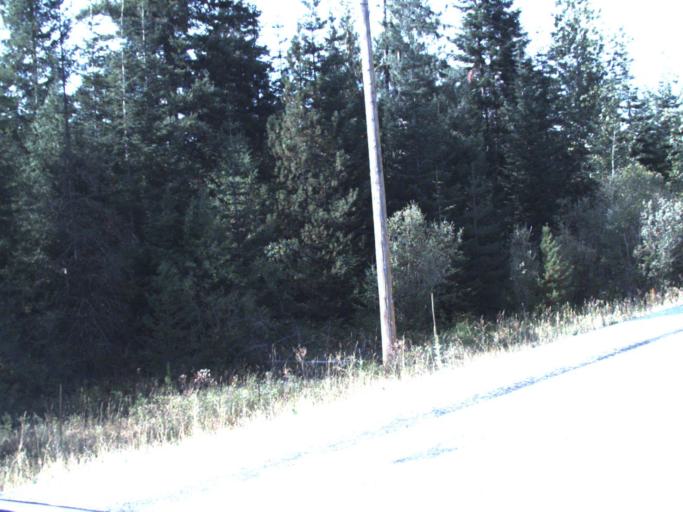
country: US
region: Washington
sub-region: Pend Oreille County
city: Newport
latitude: 48.2625
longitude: -117.2845
